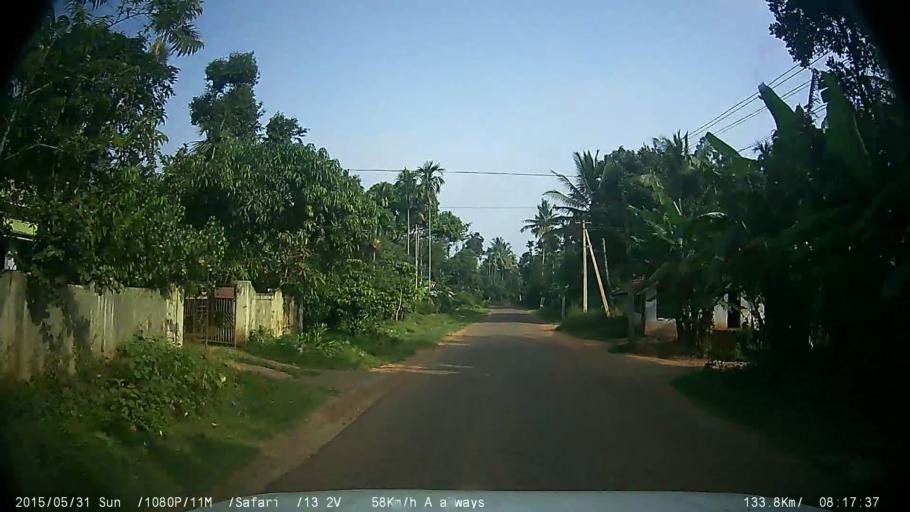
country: IN
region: Kerala
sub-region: Wayanad
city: Kalpetta
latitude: 11.6607
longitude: 75.9901
